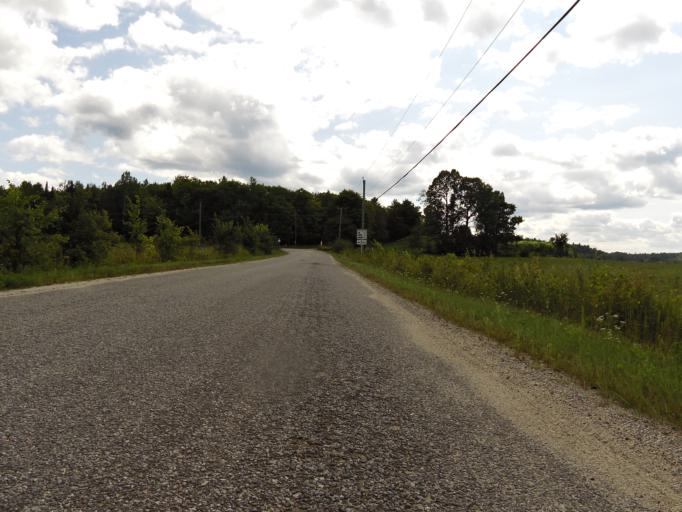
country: CA
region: Quebec
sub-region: Outaouais
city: Wakefield
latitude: 45.8048
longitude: -75.9828
